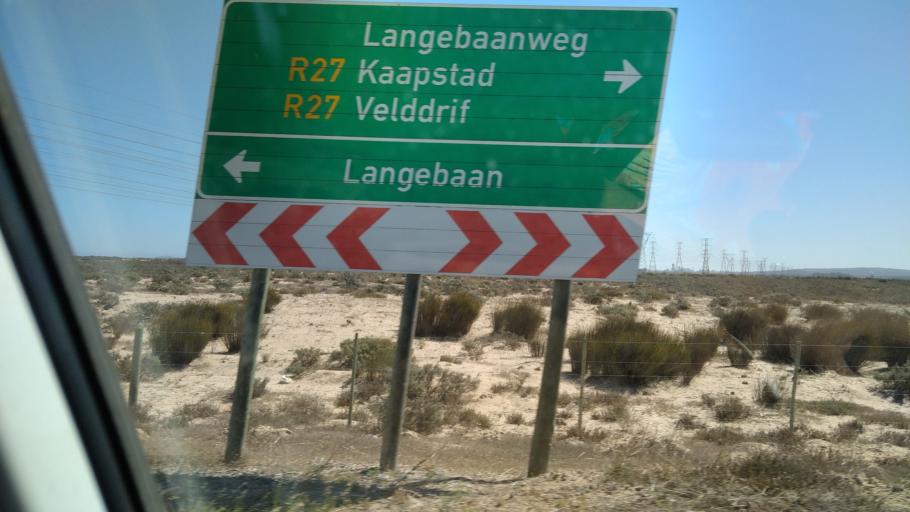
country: ZA
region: Western Cape
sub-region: West Coast District Municipality
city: Saldanha
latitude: -33.0264
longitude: 18.1043
